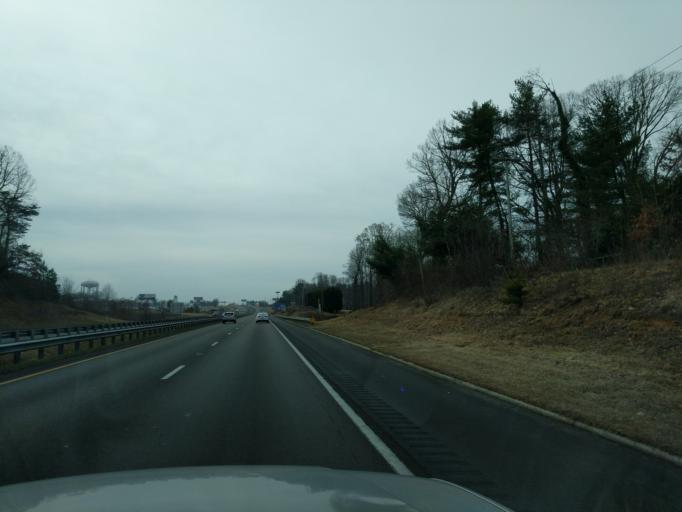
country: US
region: North Carolina
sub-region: Iredell County
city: Statesville
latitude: 35.7851
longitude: -80.8632
